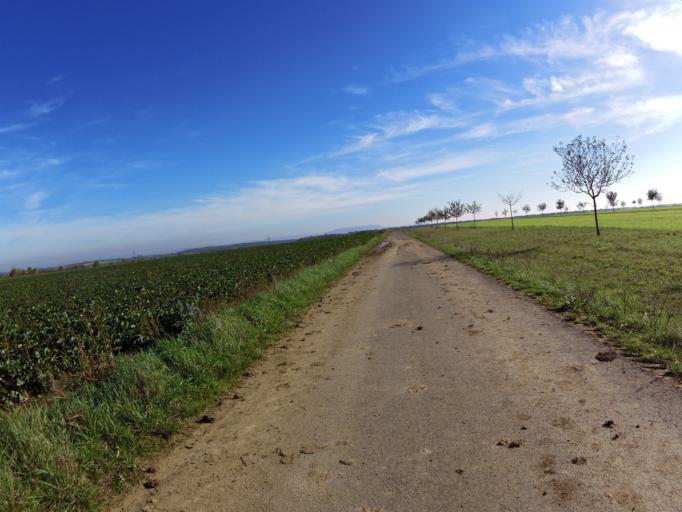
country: DE
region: Bavaria
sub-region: Regierungsbezirk Unterfranken
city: Theilheim
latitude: 49.7223
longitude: 10.0631
